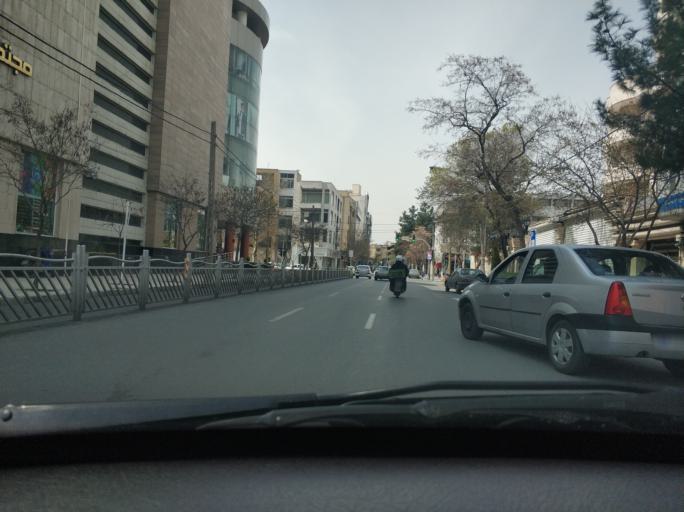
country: IR
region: Razavi Khorasan
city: Mashhad
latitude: 36.3039
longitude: 59.5724
